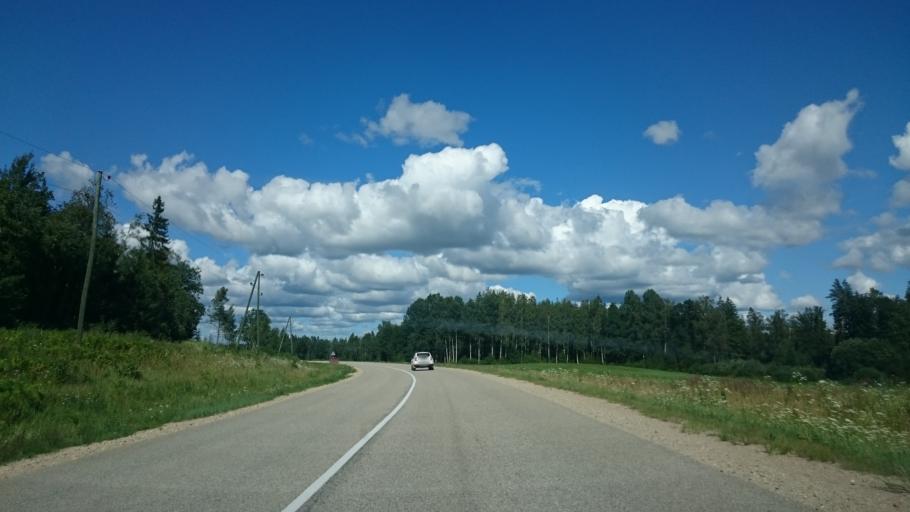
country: LV
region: Kuldigas Rajons
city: Kuldiga
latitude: 56.9070
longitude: 21.9025
